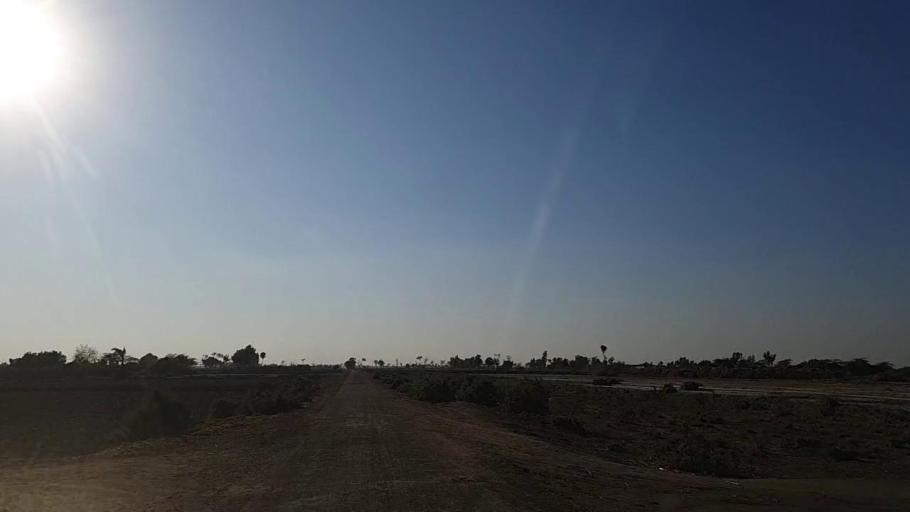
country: PK
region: Sindh
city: Samaro
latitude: 25.3442
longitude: 69.3717
